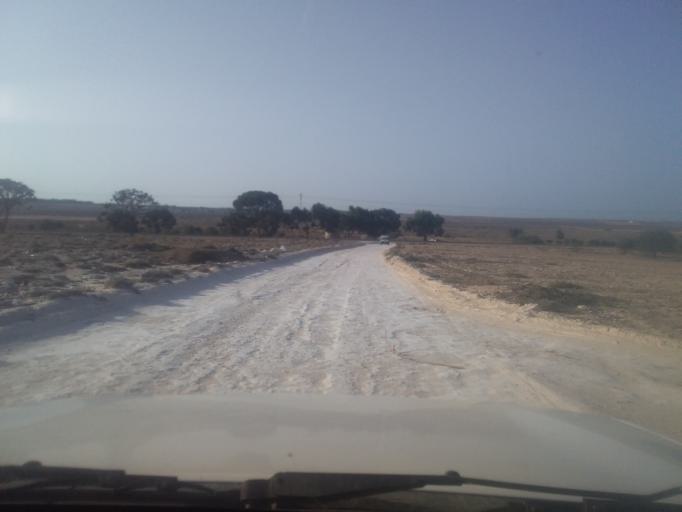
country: TN
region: Qabis
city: Gabes
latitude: 33.6398
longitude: 10.2924
